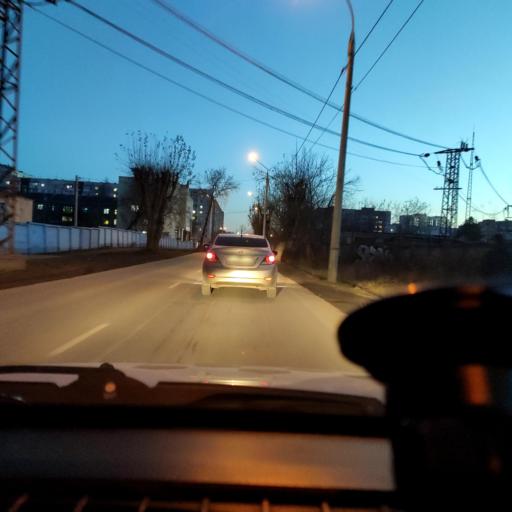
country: RU
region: Perm
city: Kondratovo
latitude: 58.0018
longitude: 56.1684
